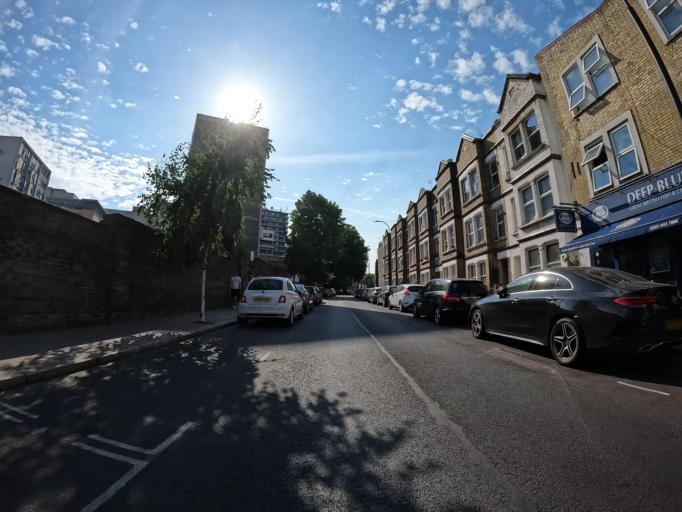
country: GB
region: England
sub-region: Greater London
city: Hendon
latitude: 51.5848
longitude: -0.2188
